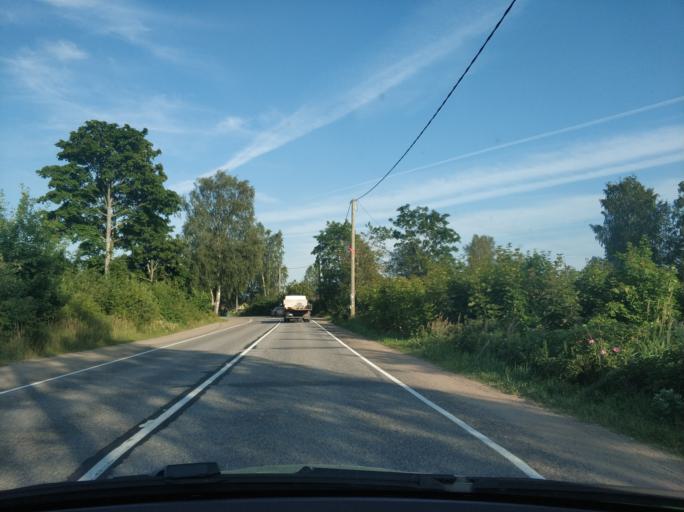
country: RU
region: Leningrad
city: Borisova Griva
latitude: 60.0940
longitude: 30.9763
